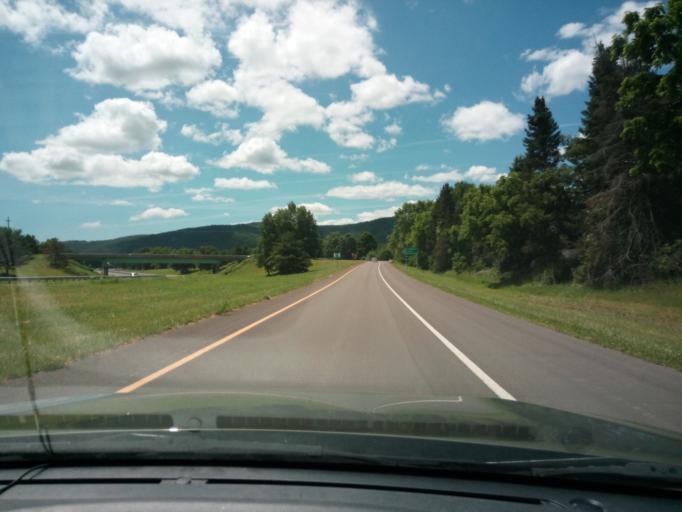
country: US
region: Pennsylvania
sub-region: Bradford County
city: South Waverly
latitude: 41.9909
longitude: -76.5493
